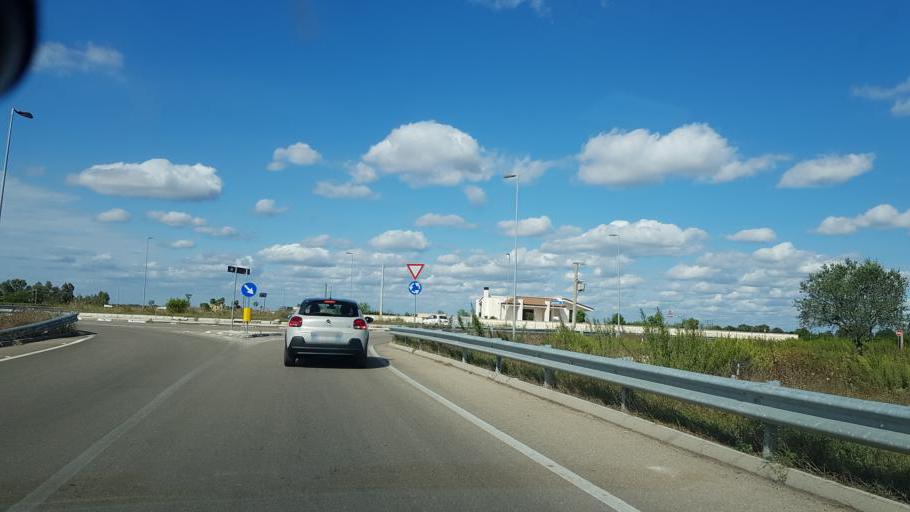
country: IT
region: Apulia
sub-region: Provincia di Lecce
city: Leverano
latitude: 40.3041
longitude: 18.0068
